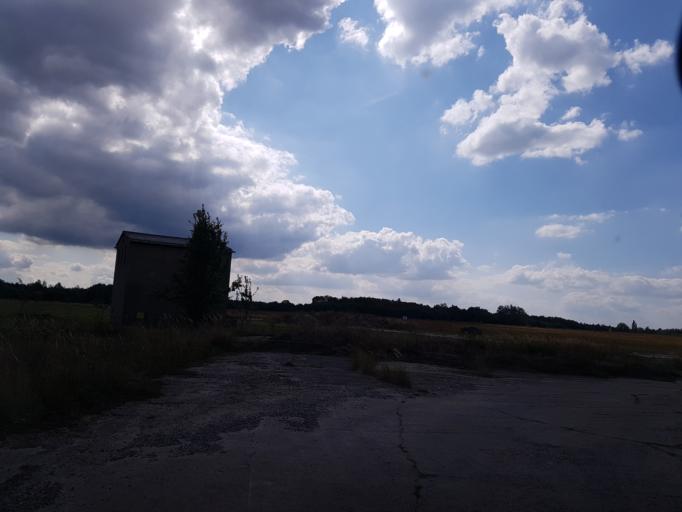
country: DE
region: Brandenburg
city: Finsterwalde
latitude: 51.6104
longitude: 13.7566
